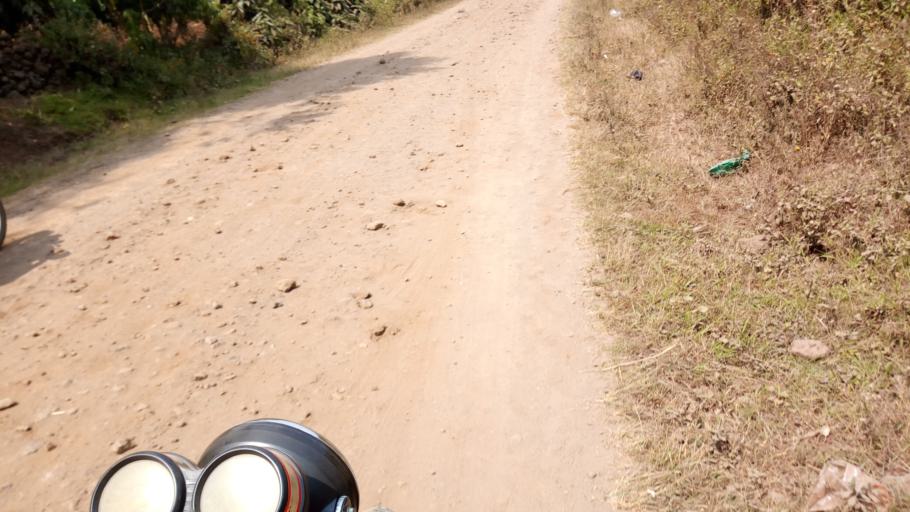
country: UG
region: Western Region
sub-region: Kisoro District
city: Kisoro
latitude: -1.3150
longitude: 29.7196
